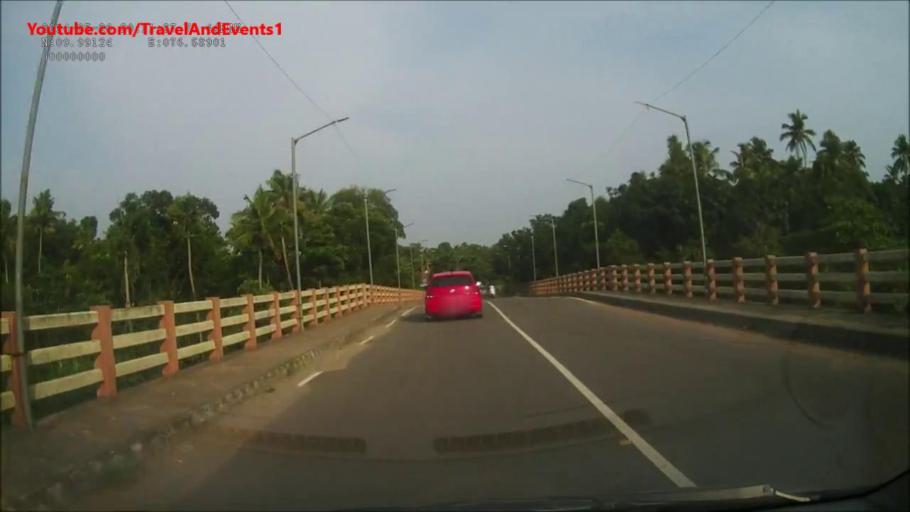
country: IN
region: Kerala
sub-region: Ernakulam
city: Muvattupula
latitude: 9.9907
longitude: 76.5895
